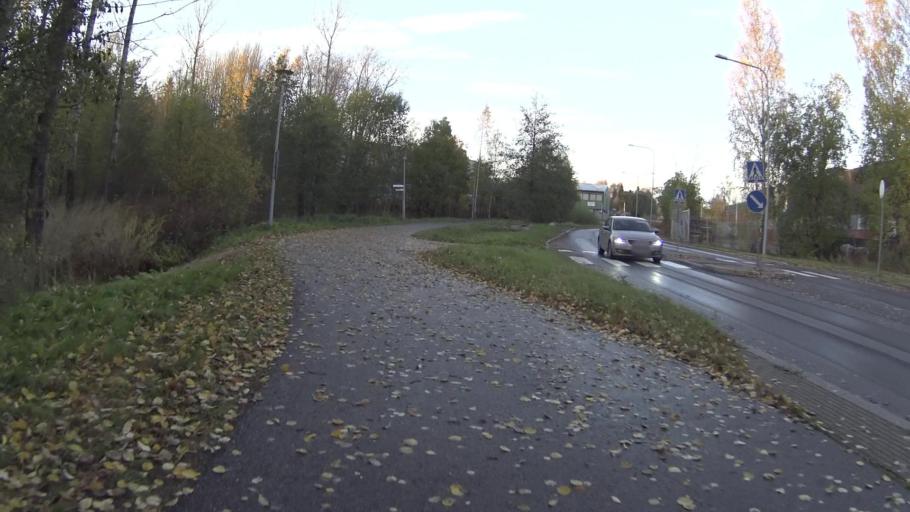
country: FI
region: Uusimaa
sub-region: Helsinki
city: Teekkarikylae
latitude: 60.2199
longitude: 24.8477
